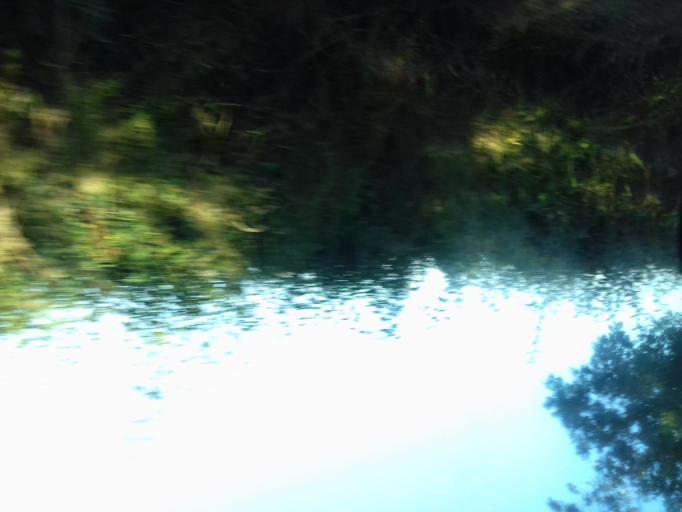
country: IE
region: Leinster
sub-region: An Mhi
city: Ashbourne
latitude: 53.4951
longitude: -6.3062
